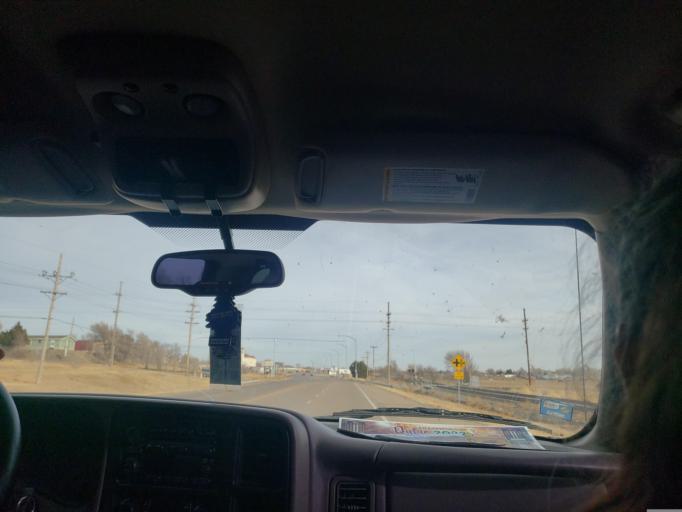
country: US
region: Kansas
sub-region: Ford County
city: Dodge City
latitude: 37.7545
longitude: -100.0527
